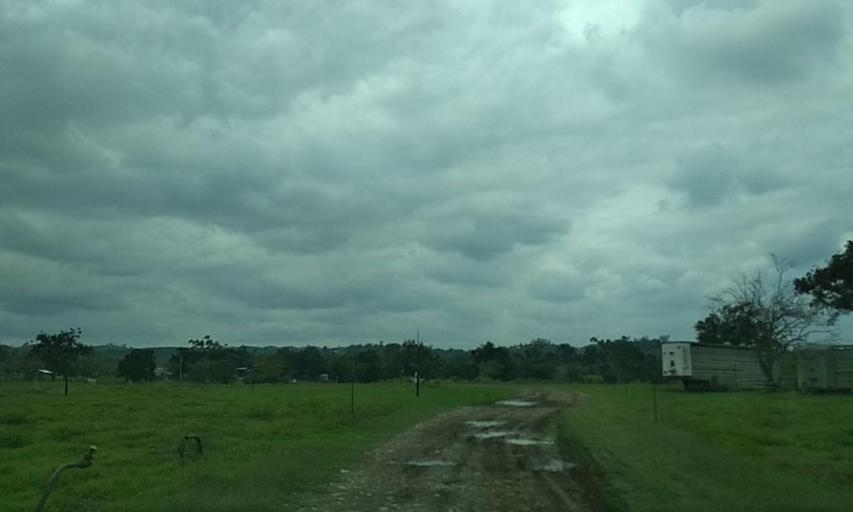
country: MX
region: Veracruz
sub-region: Papantla
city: El Chote
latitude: 20.3922
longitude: -97.3408
